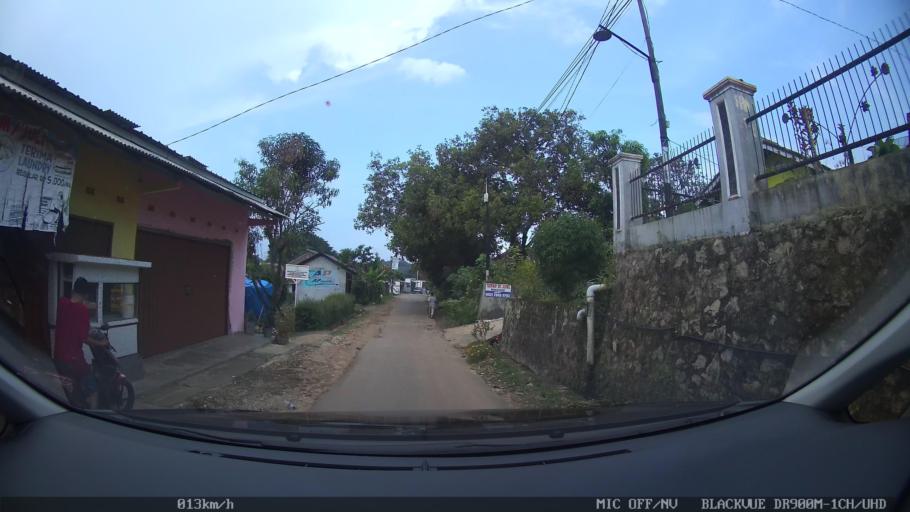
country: ID
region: Lampung
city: Kedaton
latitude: -5.3939
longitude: 105.2111
